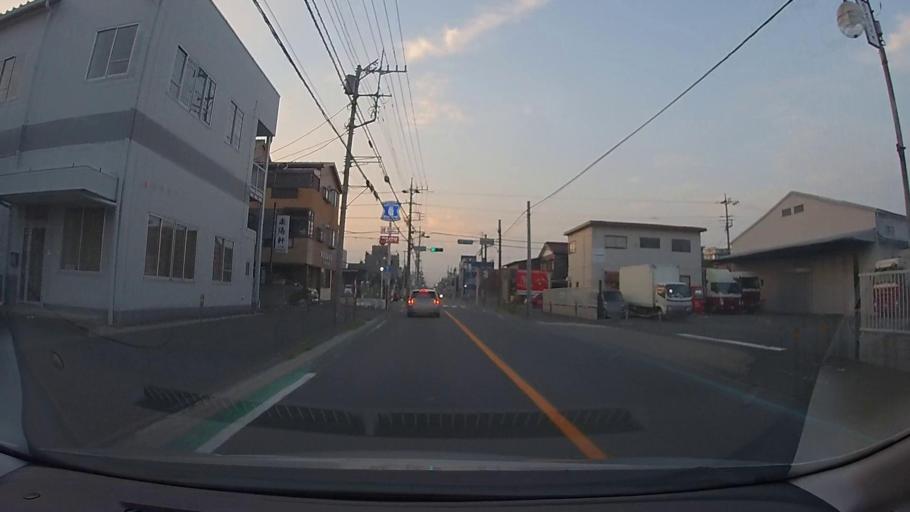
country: JP
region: Kanagawa
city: Minami-rinkan
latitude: 35.4825
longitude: 139.4513
